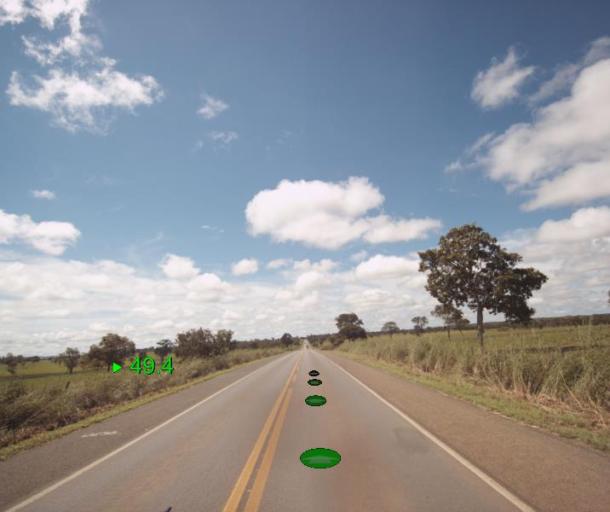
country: BR
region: Goias
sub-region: Padre Bernardo
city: Padre Bernardo
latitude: -15.1592
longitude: -48.3148
